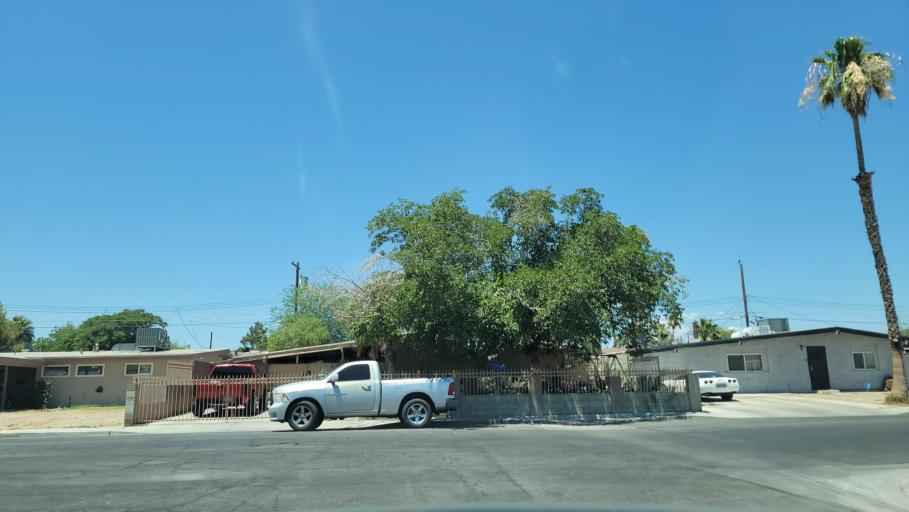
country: US
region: Nevada
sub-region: Clark County
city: Las Vegas
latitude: 36.1756
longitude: -115.1188
